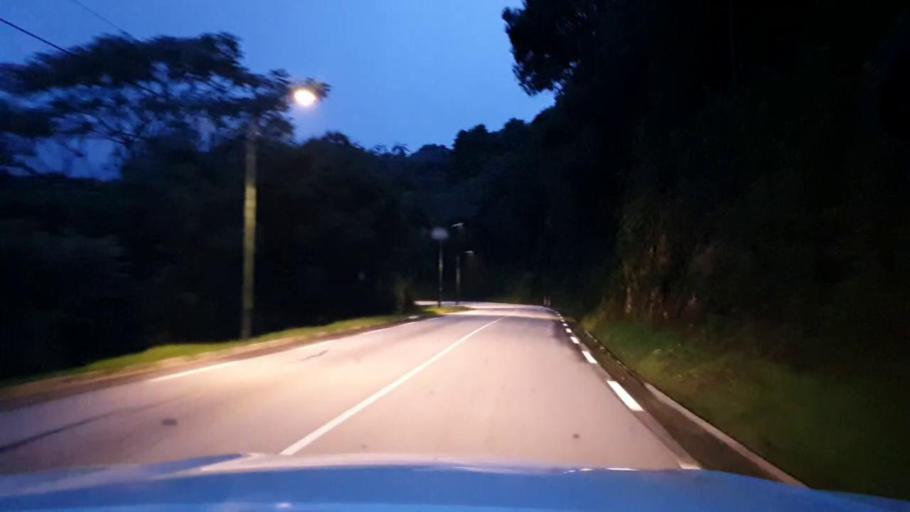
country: RW
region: Southern Province
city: Nzega
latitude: -2.5328
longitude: 29.3888
